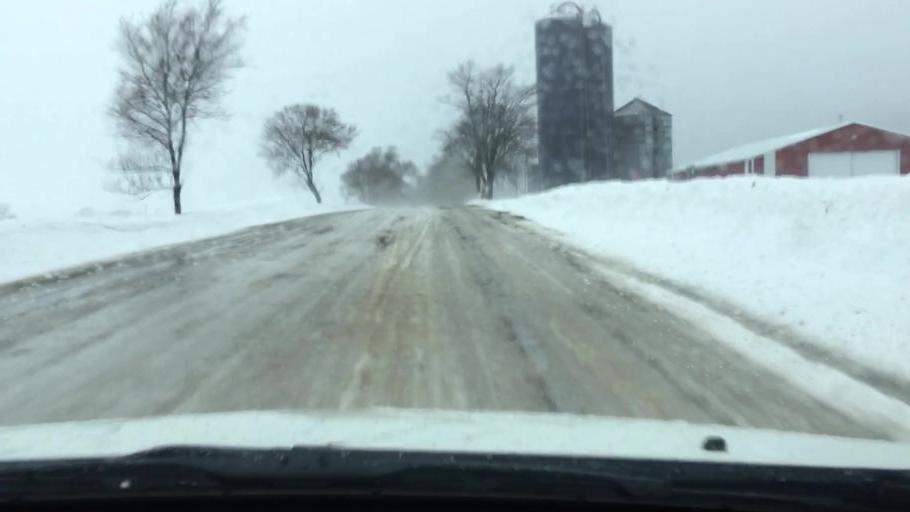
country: US
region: Michigan
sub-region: Charlevoix County
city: East Jordan
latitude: 45.1295
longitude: -85.1597
